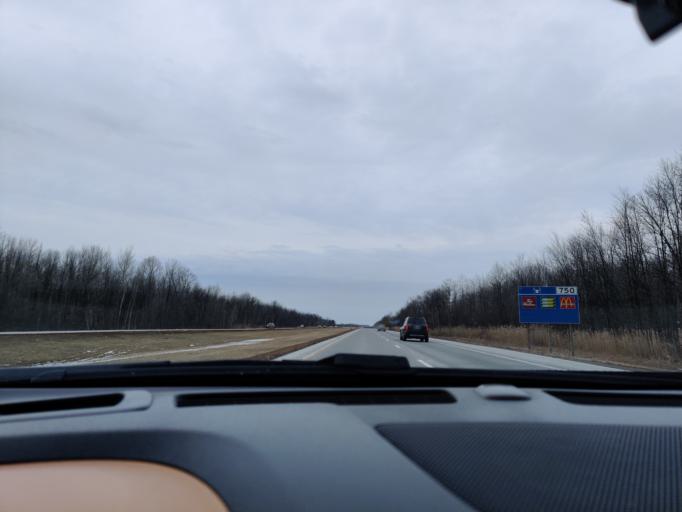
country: US
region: New York
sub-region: St. Lawrence County
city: Norfolk
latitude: 44.9292
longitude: -75.1690
